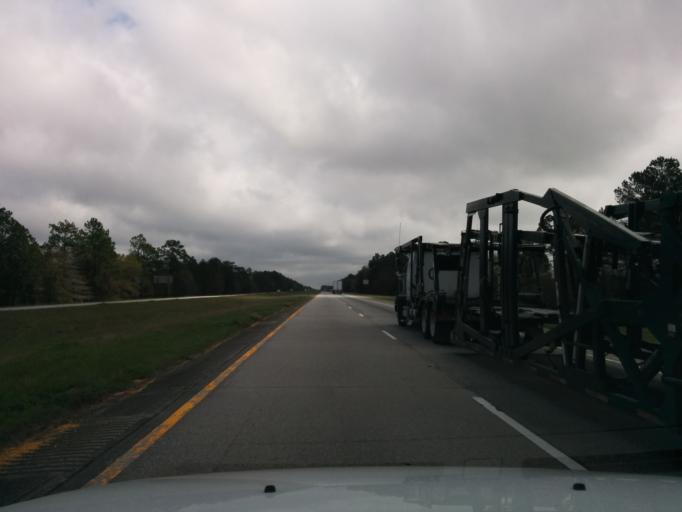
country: US
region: Georgia
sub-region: Toombs County
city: Lyons
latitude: 32.3900
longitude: -82.2847
